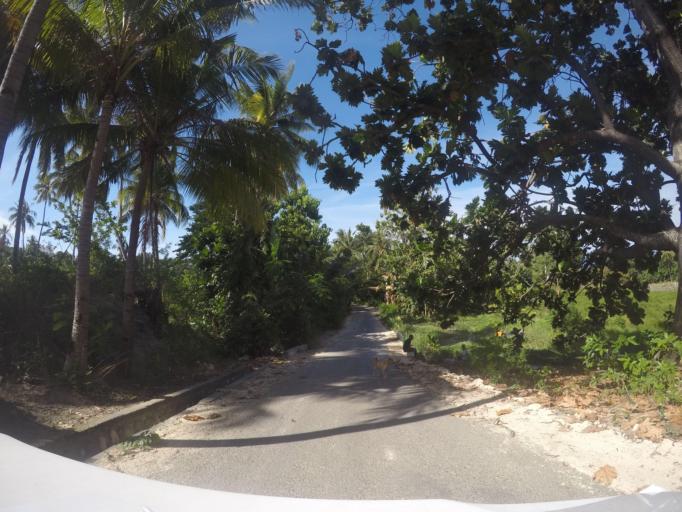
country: TL
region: Baucau
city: Baucau
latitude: -8.4538
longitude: 126.4580
